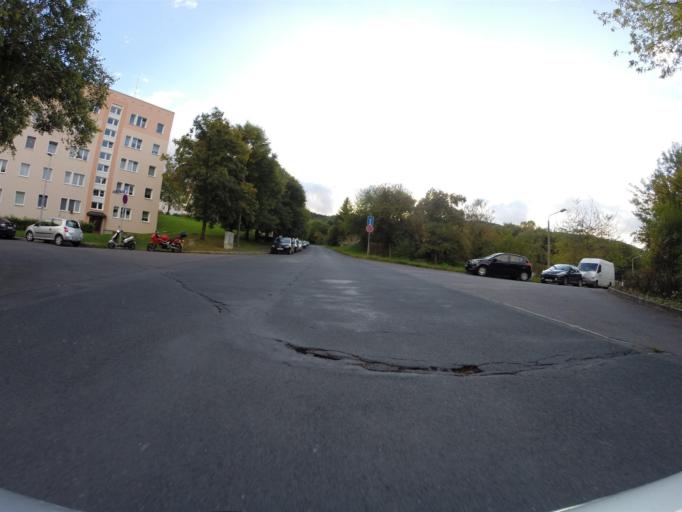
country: DE
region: Thuringia
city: Jena
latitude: 50.8921
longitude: 11.5773
